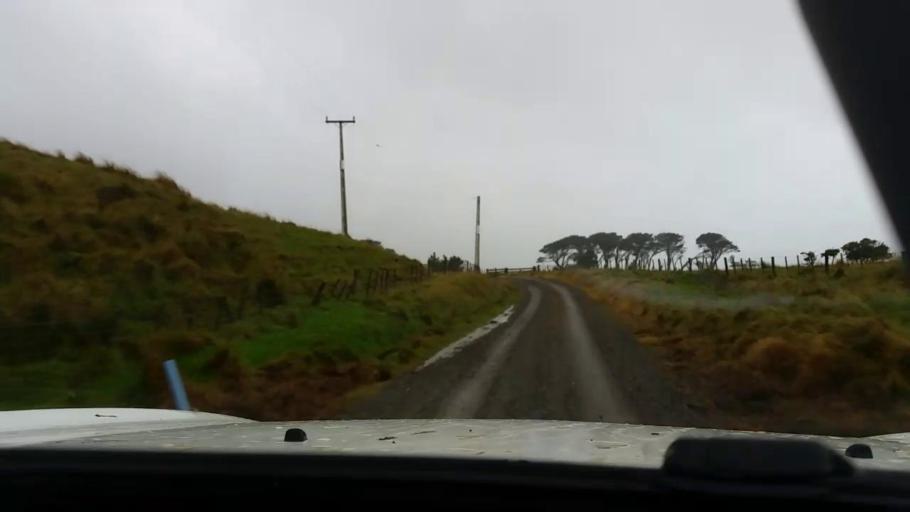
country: NZ
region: Wellington
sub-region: Masterton District
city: Masterton
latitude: -41.2639
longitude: 175.8925
